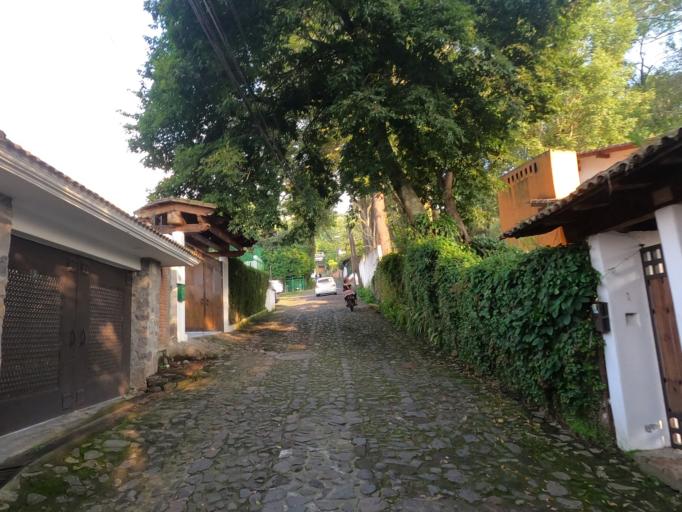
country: MX
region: Mexico
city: Valle de Bravo
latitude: 19.1972
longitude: -100.1288
